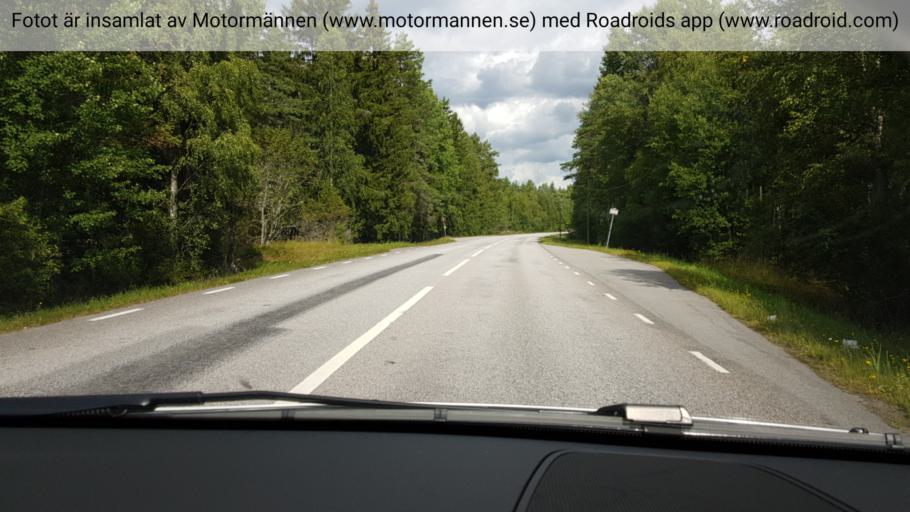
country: SE
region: Stockholm
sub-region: Sigtuna Kommun
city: Marsta
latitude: 59.7824
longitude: 18.0387
